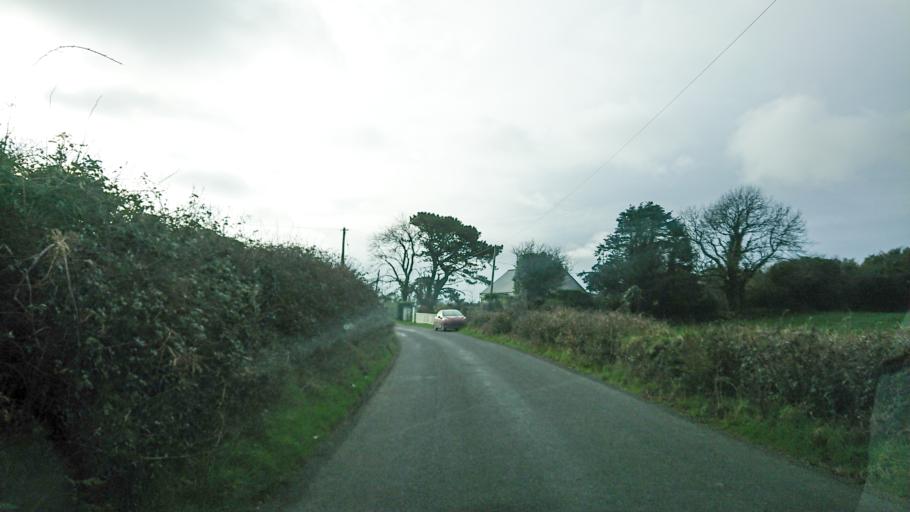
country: IE
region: Munster
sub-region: Waterford
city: Tra Mhor
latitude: 52.1746
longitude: -7.1760
